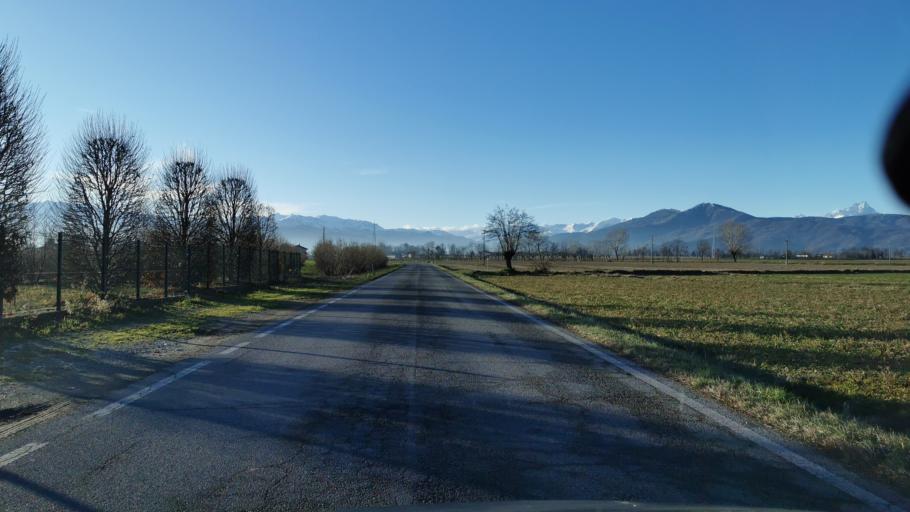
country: IT
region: Piedmont
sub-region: Provincia di Cuneo
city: Roata Rossi
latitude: 44.4580
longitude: 7.5073
